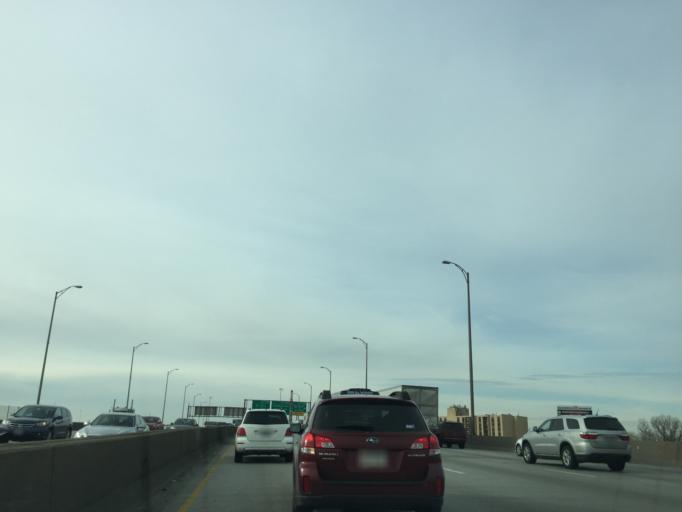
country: US
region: Illinois
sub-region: Cook County
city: Chicago
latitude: 41.8455
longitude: -87.6351
